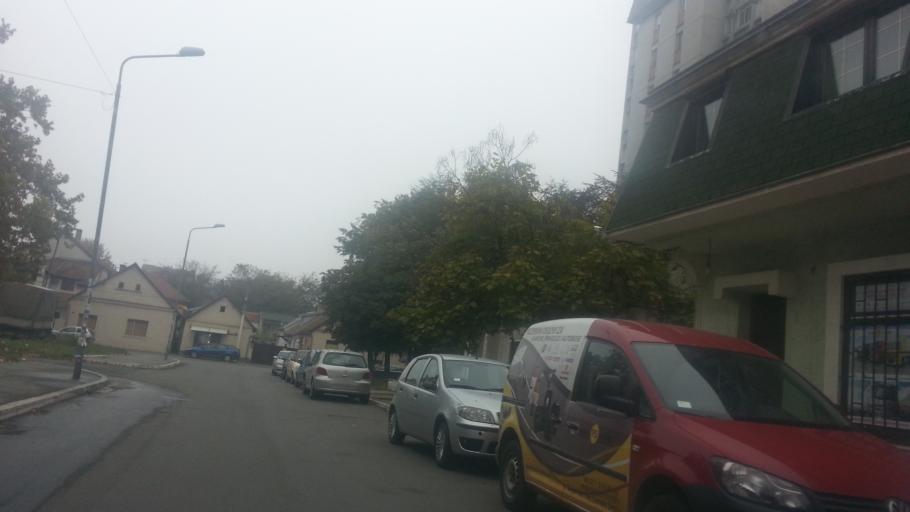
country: RS
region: Central Serbia
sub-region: Belgrade
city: Zemun
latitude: 44.8455
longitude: 20.3848
